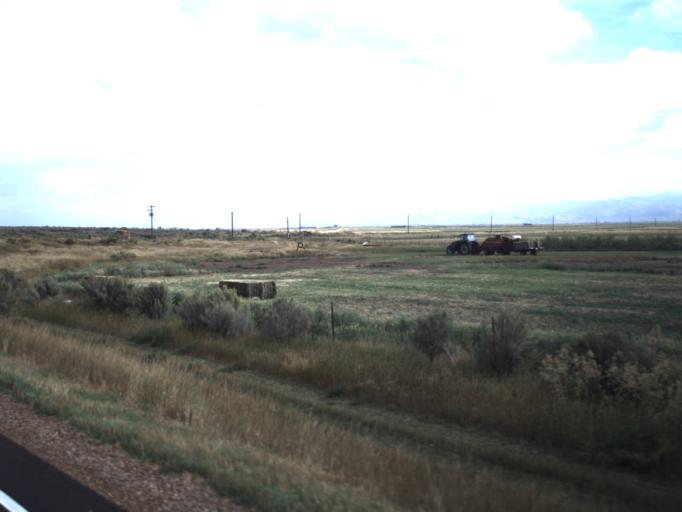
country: US
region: Utah
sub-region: Rich County
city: Randolph
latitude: 41.6868
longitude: -111.1778
